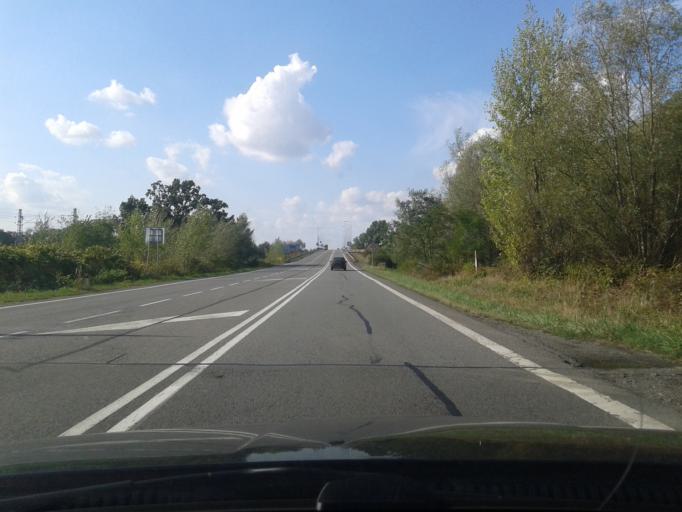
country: CZ
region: Moravskoslezsky
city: Stary Bohumin
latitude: 49.9137
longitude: 18.3278
